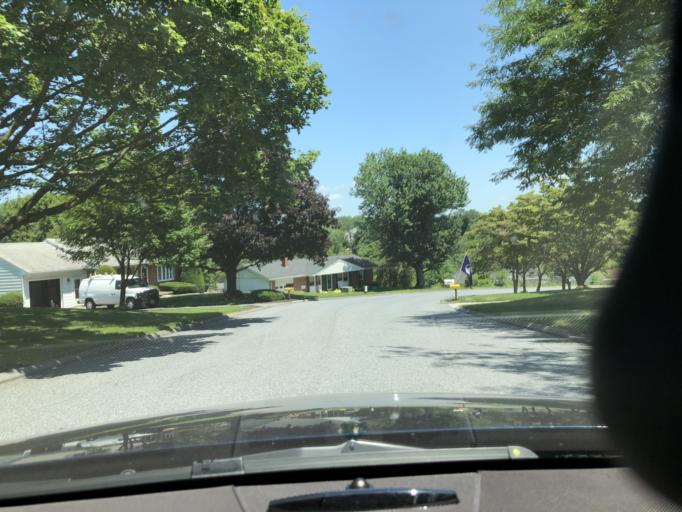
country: US
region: Maryland
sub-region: Carroll County
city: Westminster
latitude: 39.5548
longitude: -76.9674
